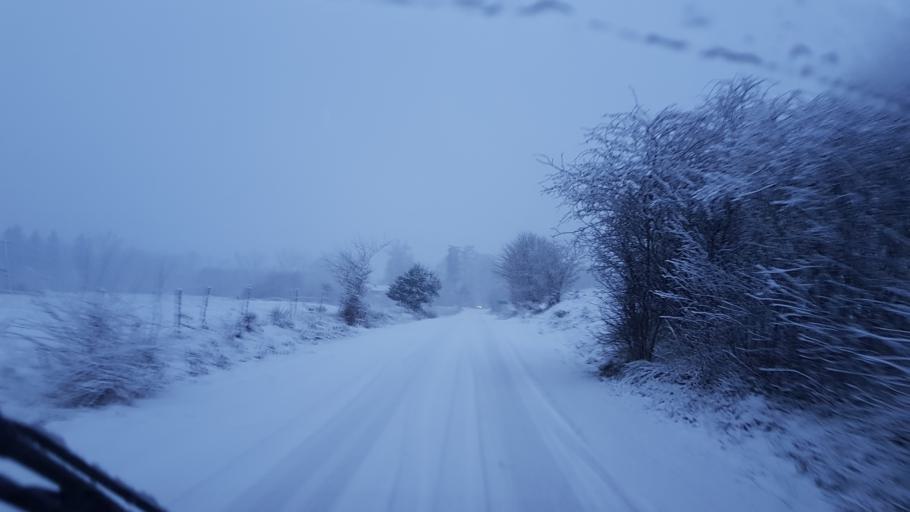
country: PL
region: West Pomeranian Voivodeship
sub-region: Powiat koszalinski
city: Sianow
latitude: 54.1630
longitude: 16.4519
